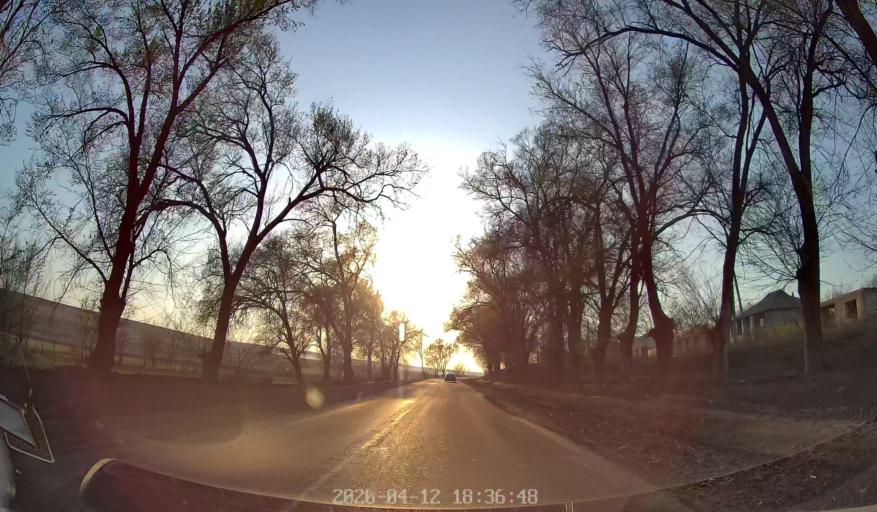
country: MD
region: Chisinau
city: Vadul lui Voda
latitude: 47.1177
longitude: 29.0241
